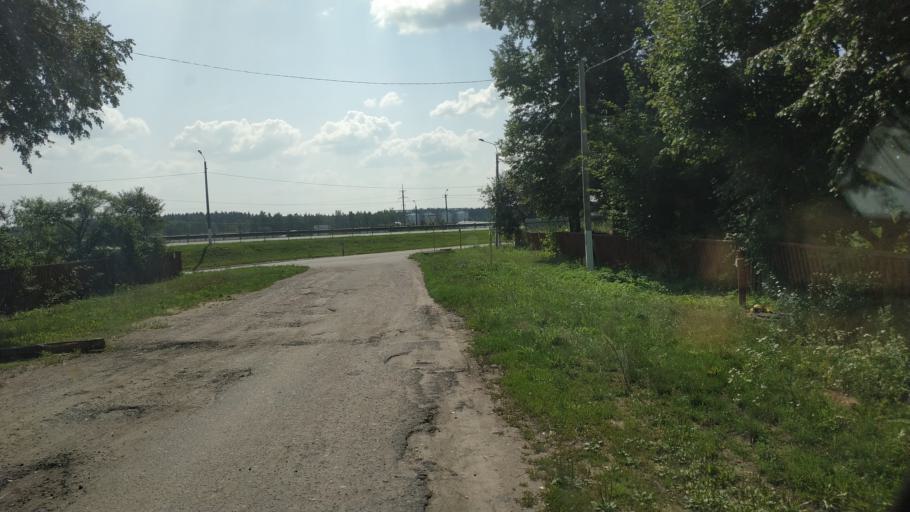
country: BY
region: Mogilev
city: Buynichy
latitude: 53.9632
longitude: 30.1875
